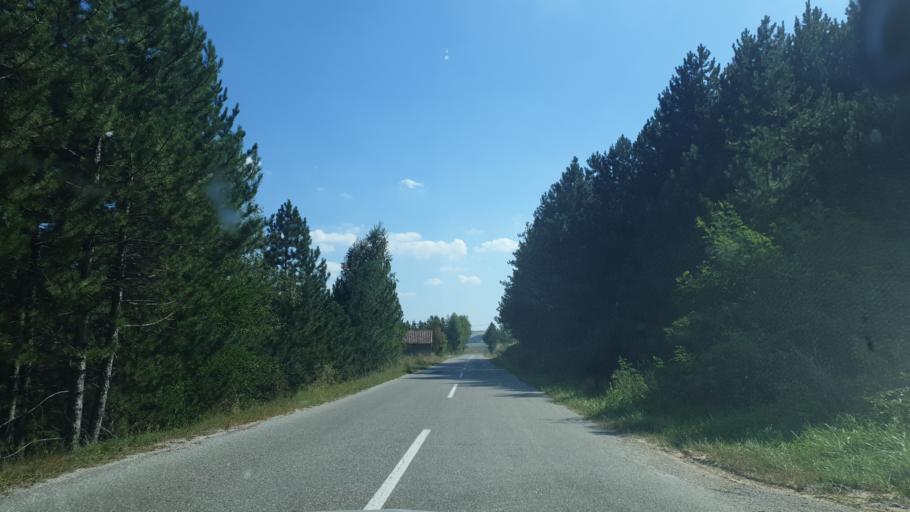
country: RS
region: Central Serbia
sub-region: Zlatiborski Okrug
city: Kosjeric
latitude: 44.0698
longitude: 20.0184
